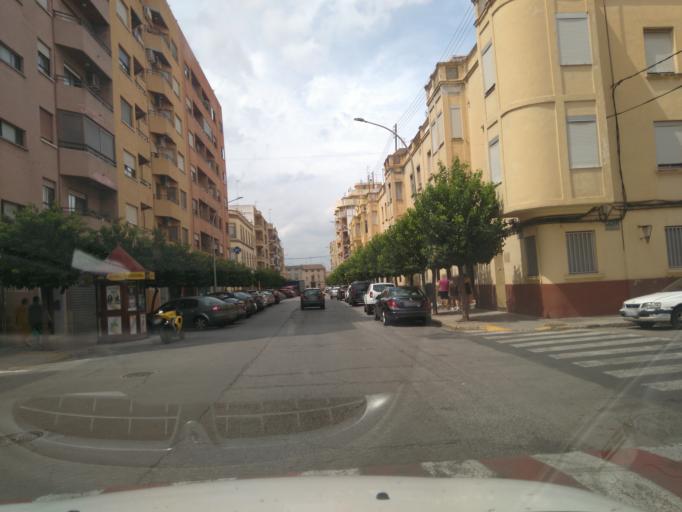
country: ES
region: Valencia
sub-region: Provincia de Valencia
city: Carcaixent
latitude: 39.1245
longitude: -0.4478
